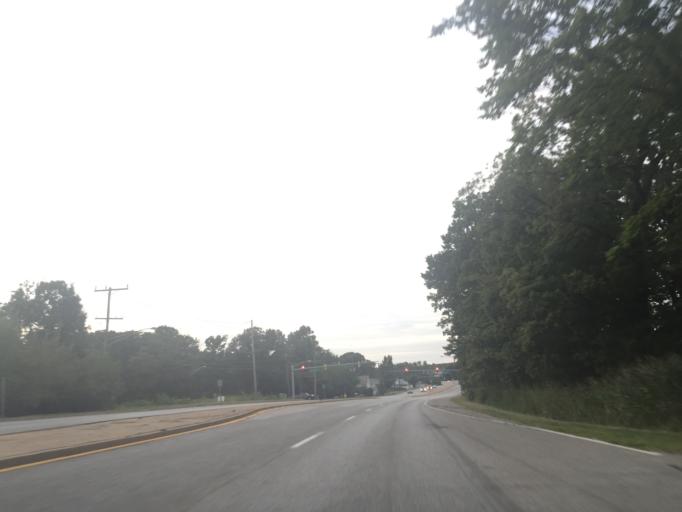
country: US
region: Maryland
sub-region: Anne Arundel County
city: Riviera Beach
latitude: 39.1918
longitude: -76.5543
